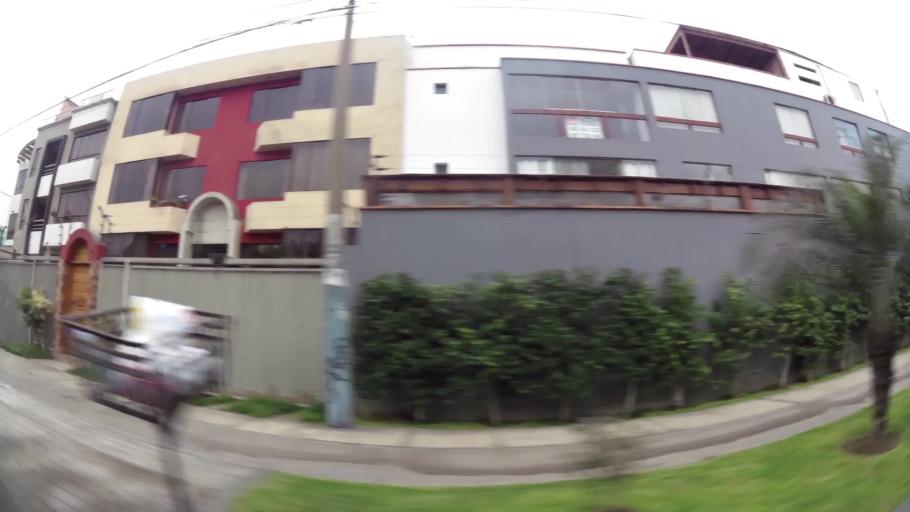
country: PE
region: Lima
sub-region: Lima
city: La Molina
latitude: -12.0942
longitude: -76.9462
